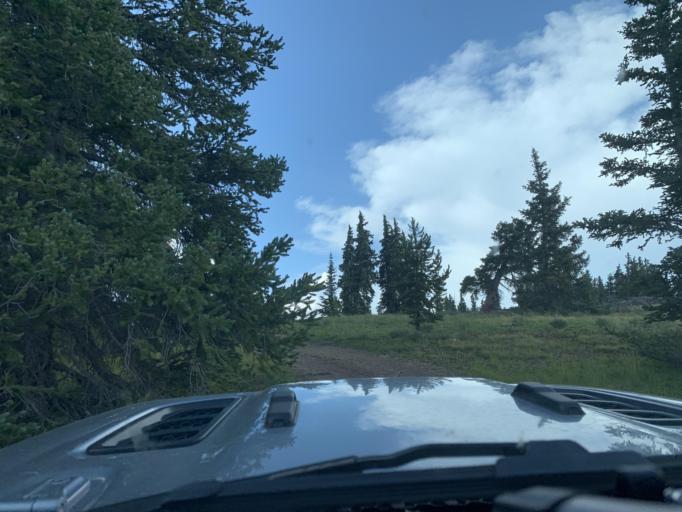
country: US
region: Colorado
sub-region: Lake County
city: Leadville North
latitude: 39.3078
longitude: -106.2889
